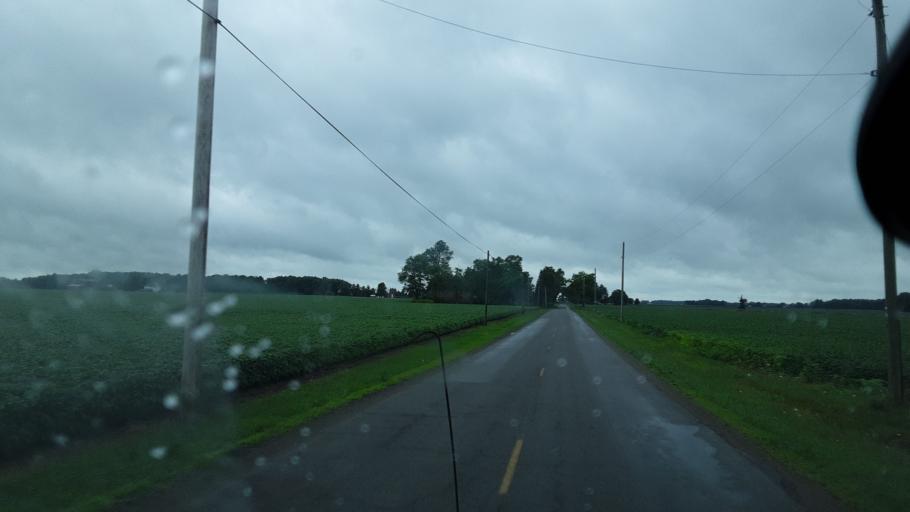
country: US
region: Ohio
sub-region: Van Wert County
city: Van Wert
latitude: 40.8005
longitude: -84.6208
